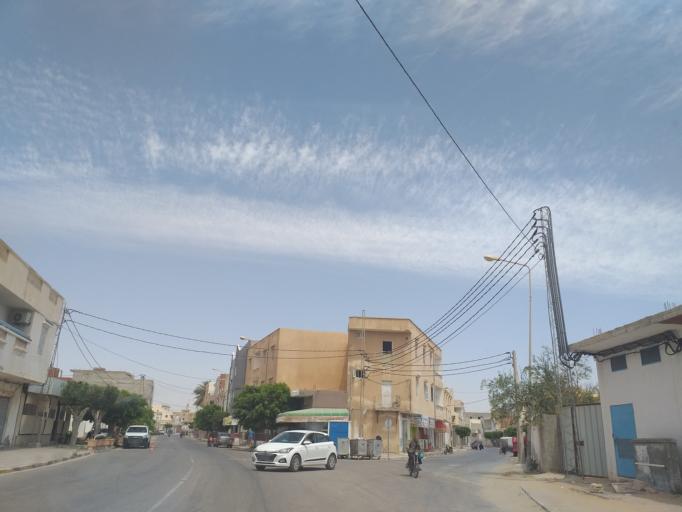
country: TN
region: Qabis
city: Gabes
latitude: 33.9357
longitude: 10.0694
